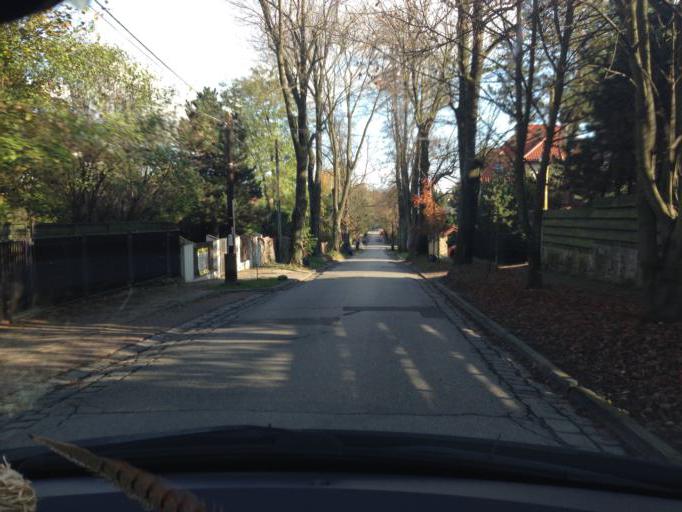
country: PL
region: Lesser Poland Voivodeship
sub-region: Powiat krakowski
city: Rzaska
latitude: 50.0664
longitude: 19.8583
